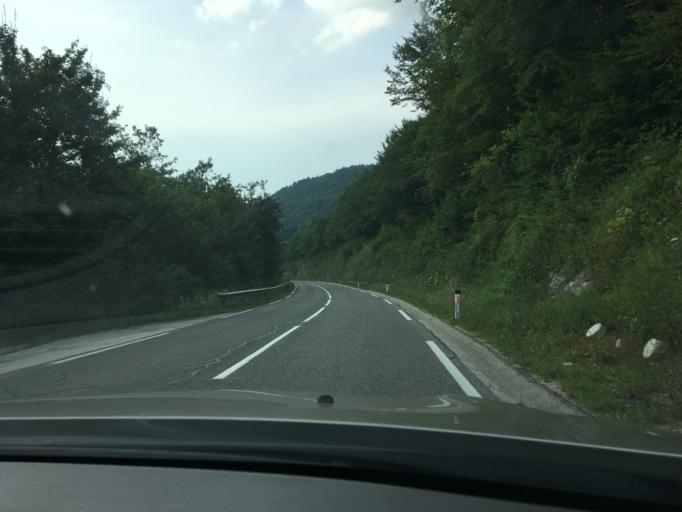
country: SI
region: Zuzemberk
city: Zuzemberk
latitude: 45.7912
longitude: 14.9888
